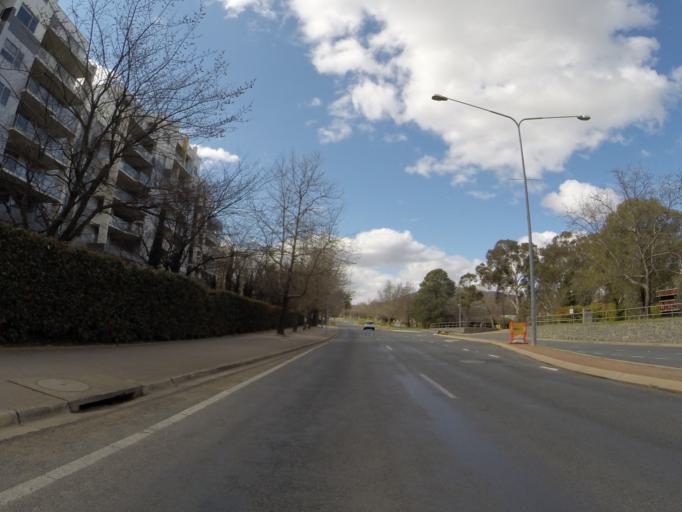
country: AU
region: Australian Capital Territory
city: Canberra
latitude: -35.2849
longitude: 149.1357
